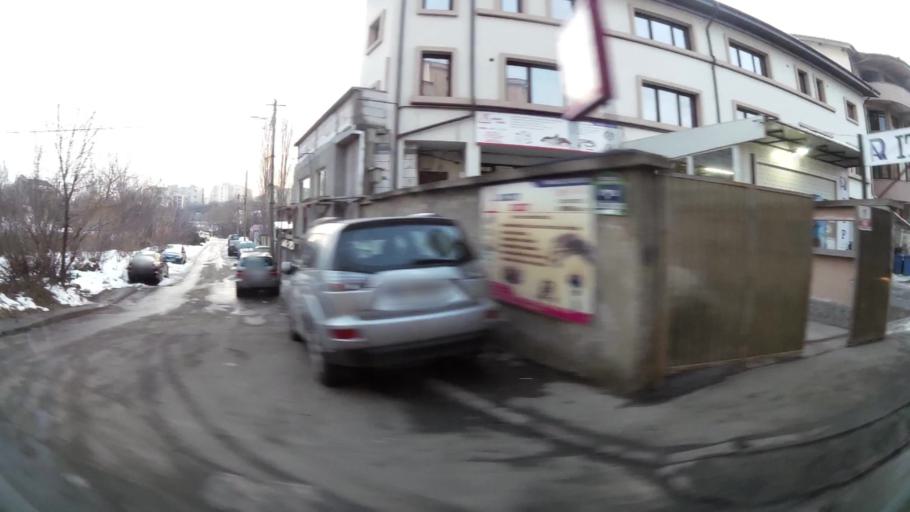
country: RO
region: Ilfov
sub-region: Comuna Fundeni-Dobroesti
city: Fundeni
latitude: 44.4628
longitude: 26.1416
